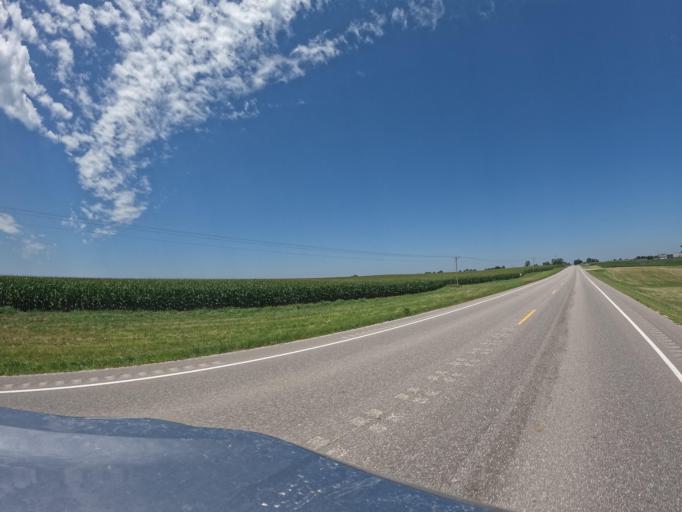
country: US
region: Iowa
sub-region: Keokuk County
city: Sigourney
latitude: 41.4194
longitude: -92.3548
